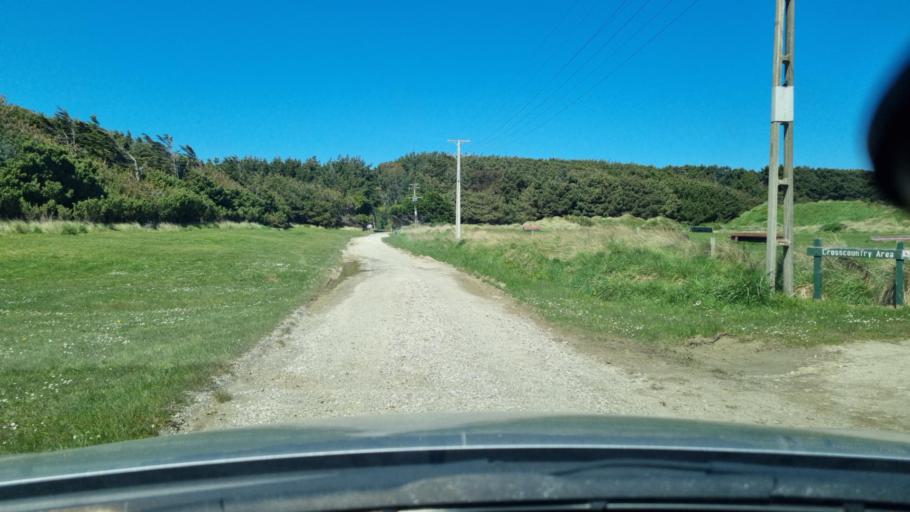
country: NZ
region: Southland
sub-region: Invercargill City
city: Invercargill
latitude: -46.4397
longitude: 168.2394
